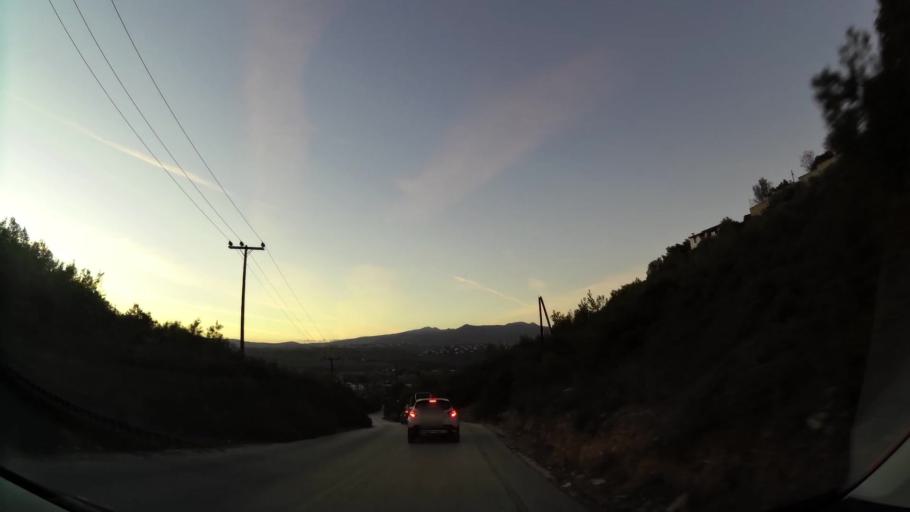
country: GR
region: Attica
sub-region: Nomarchia Anatolikis Attikis
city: Rafina
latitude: 38.0052
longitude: 23.9788
